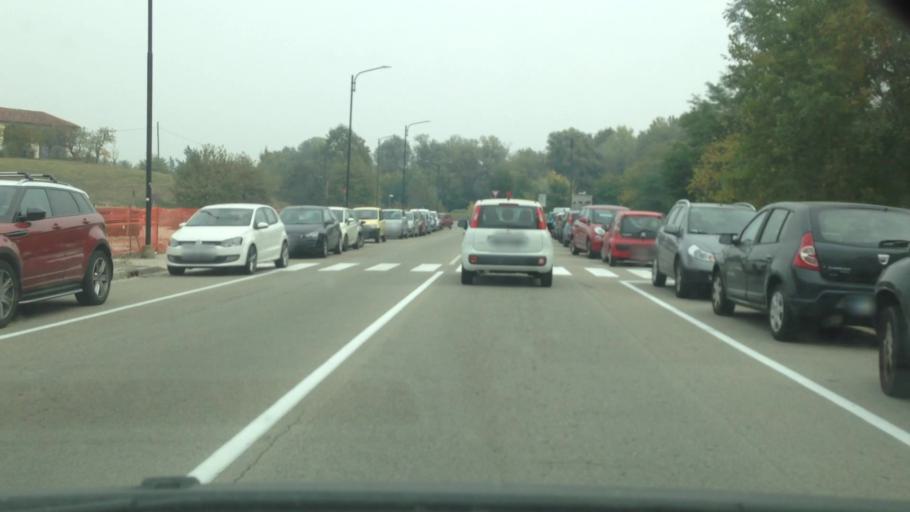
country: IT
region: Piedmont
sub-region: Provincia di Asti
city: Asti
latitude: 44.9141
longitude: 8.1945
